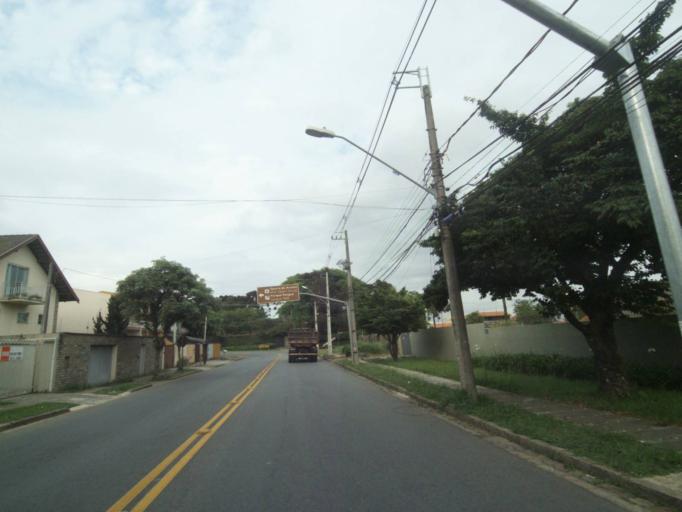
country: BR
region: Parana
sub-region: Curitiba
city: Curitiba
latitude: -25.4020
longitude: -49.2875
